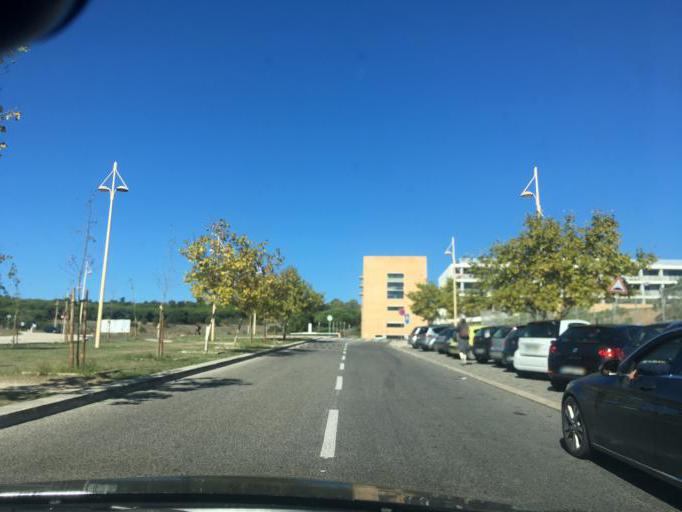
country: PT
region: Lisbon
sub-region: Oeiras
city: Alges
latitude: 38.7127
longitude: -9.1955
